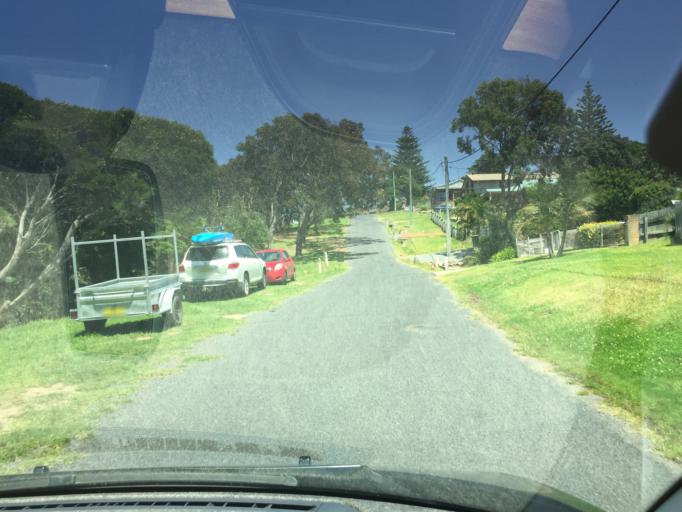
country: AU
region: New South Wales
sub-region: Bega Valley
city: Bega
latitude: -36.7345
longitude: 149.9853
